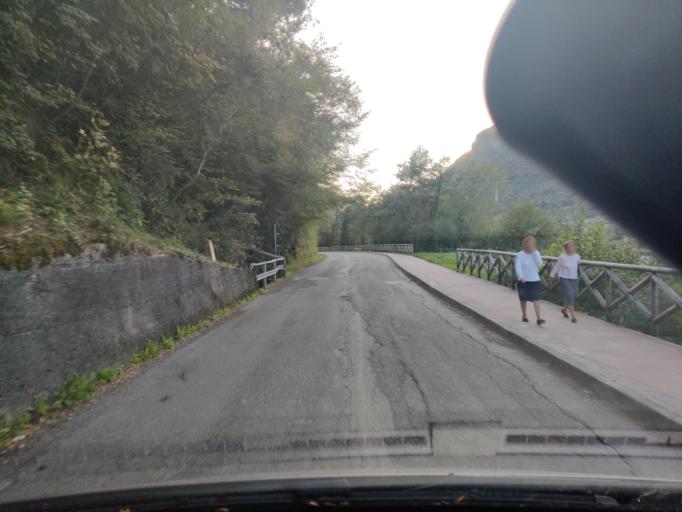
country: IT
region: Lombardy
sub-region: Provincia di Brescia
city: Anfo
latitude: 45.7504
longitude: 10.4884
